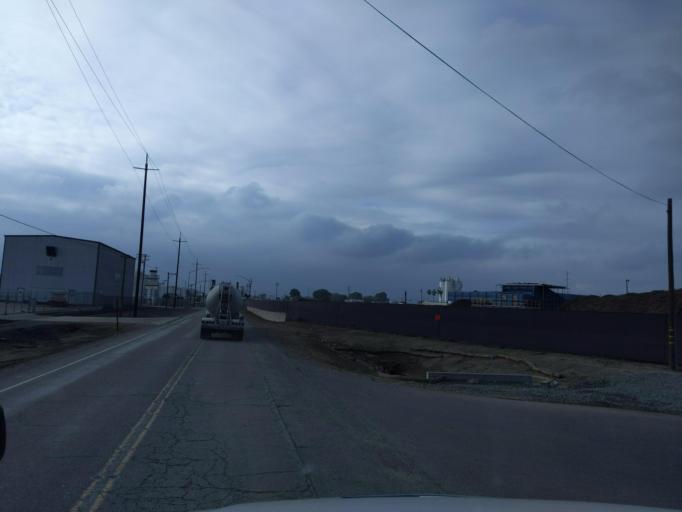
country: US
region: California
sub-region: San Joaquin County
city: Country Club
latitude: 37.9445
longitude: -121.3302
